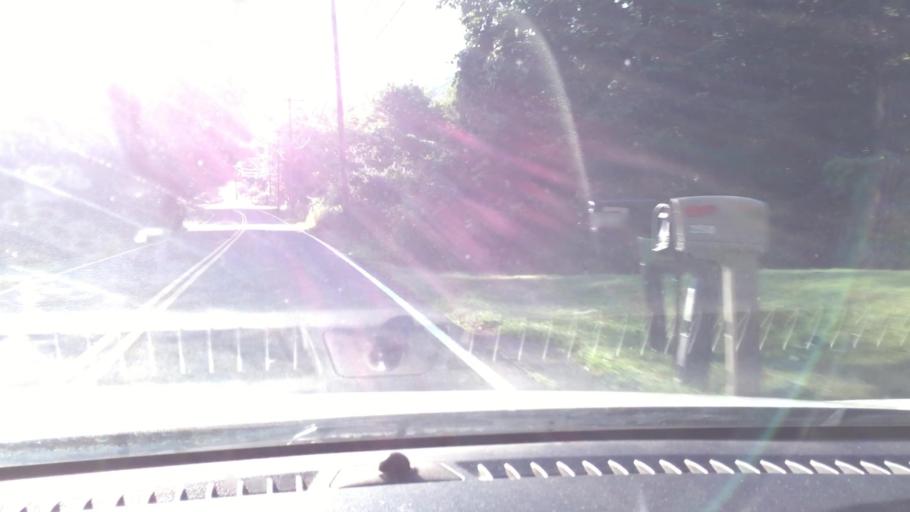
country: US
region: Massachusetts
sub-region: Berkshire County
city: Pittsfield
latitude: 42.3935
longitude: -73.2375
